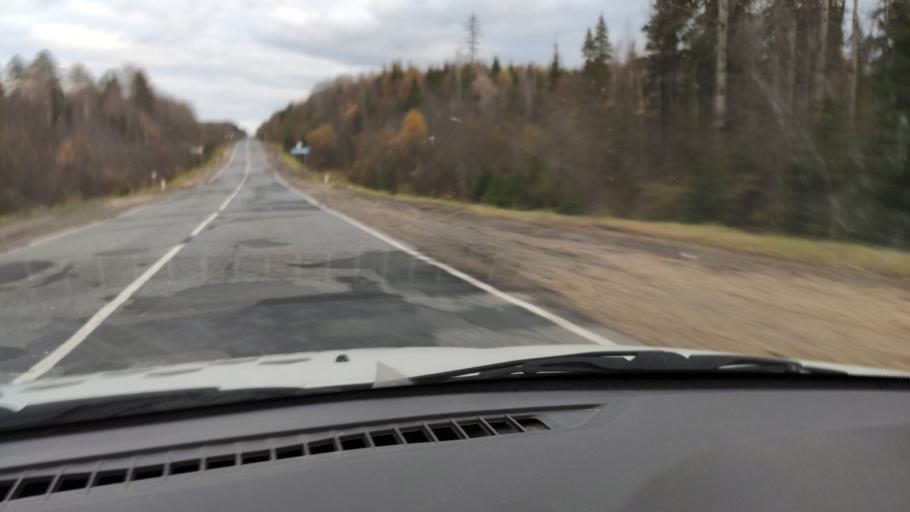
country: RU
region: Kirov
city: Chernaya Kholunitsa
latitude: 58.8906
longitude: 51.3524
